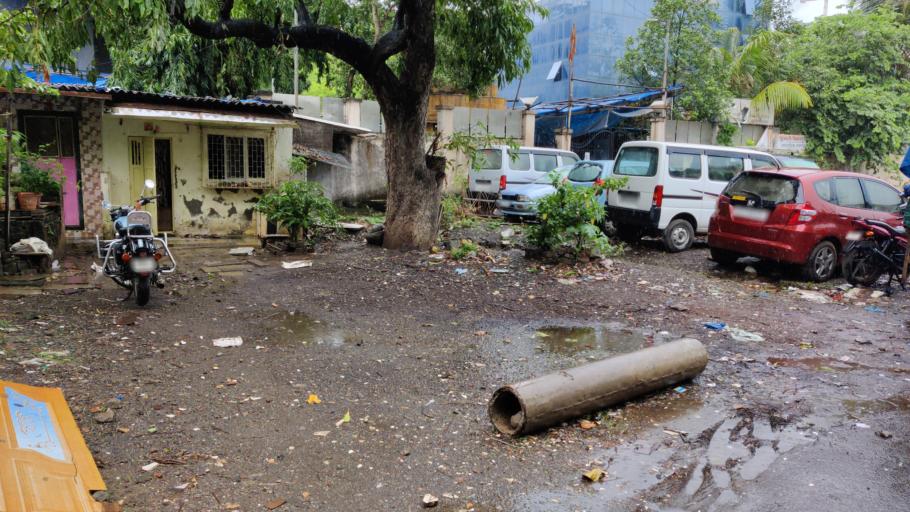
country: IN
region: Maharashtra
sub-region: Mumbai Suburban
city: Borivli
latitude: 19.2443
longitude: 72.8655
